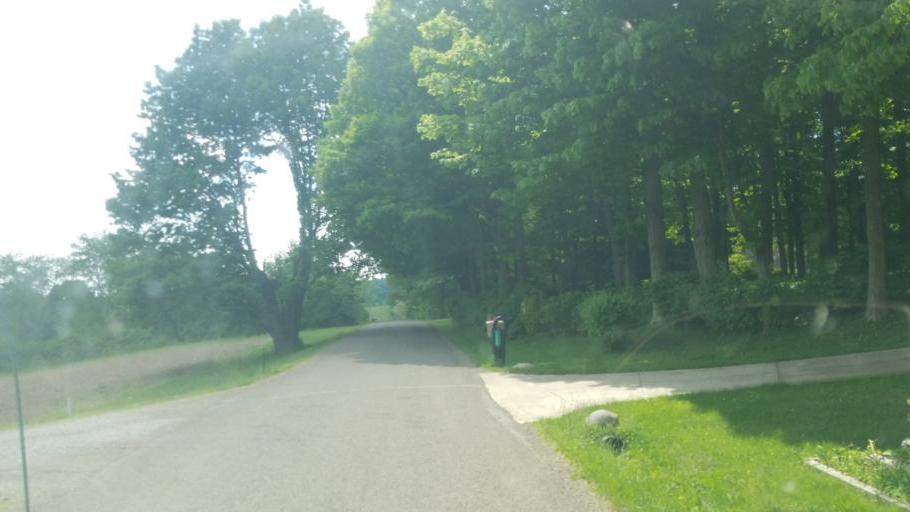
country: US
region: Ohio
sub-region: Sandusky County
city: Bellville
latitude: 40.6600
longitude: -82.4620
